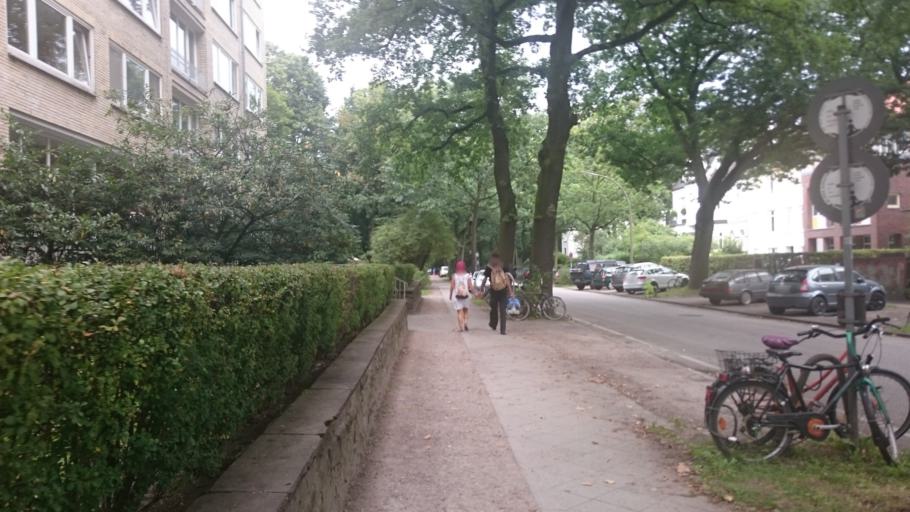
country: DE
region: Hamburg
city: Eimsbuettel
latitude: 53.5759
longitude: 9.9817
